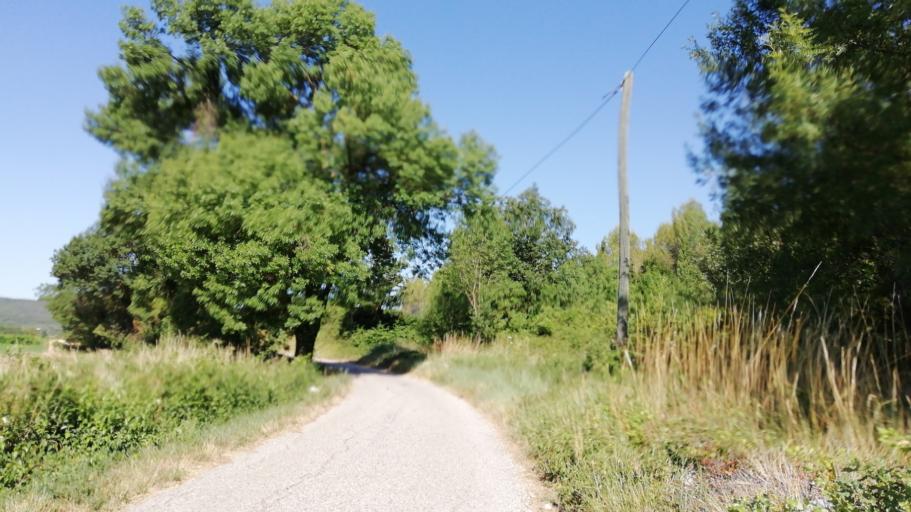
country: FR
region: Languedoc-Roussillon
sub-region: Departement de l'Herault
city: Saint-Martin-de-Londres
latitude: 43.7894
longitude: 3.7453
